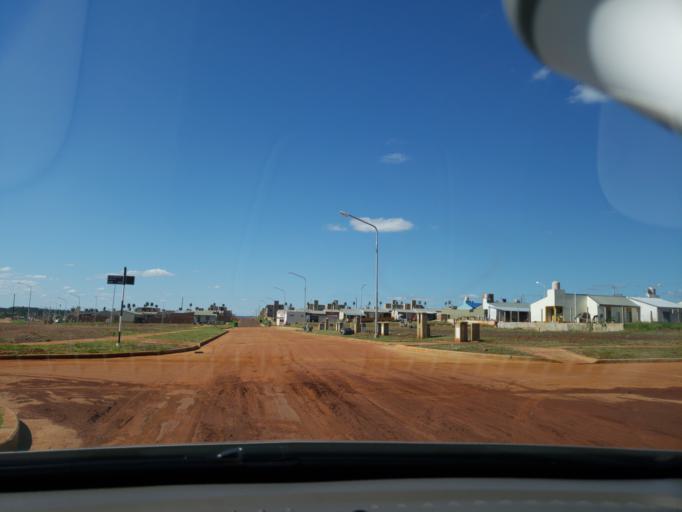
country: AR
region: Misiones
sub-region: Departamento de Capital
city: Posadas
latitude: -27.4055
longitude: -55.9872
